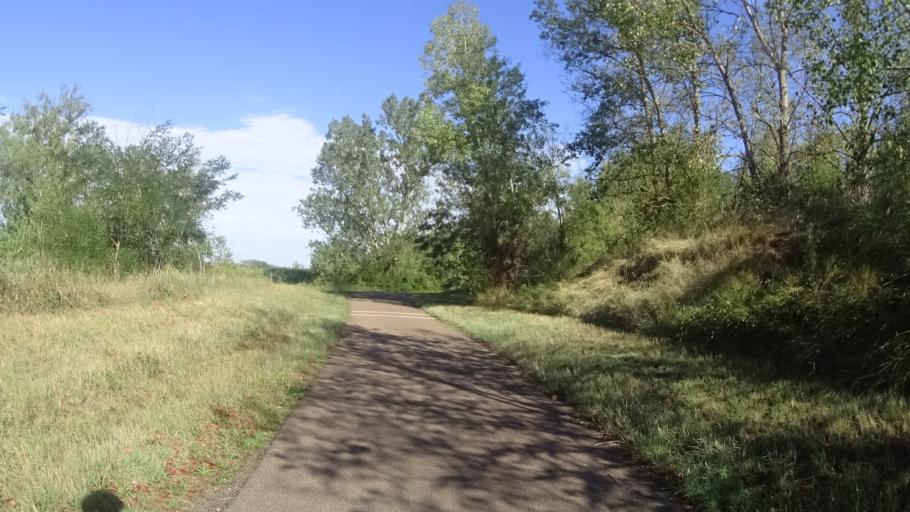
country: FR
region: Bourgogne
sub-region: Departement de la Nievre
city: Pouilly-sur-Loire
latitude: 47.3037
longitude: 2.9142
